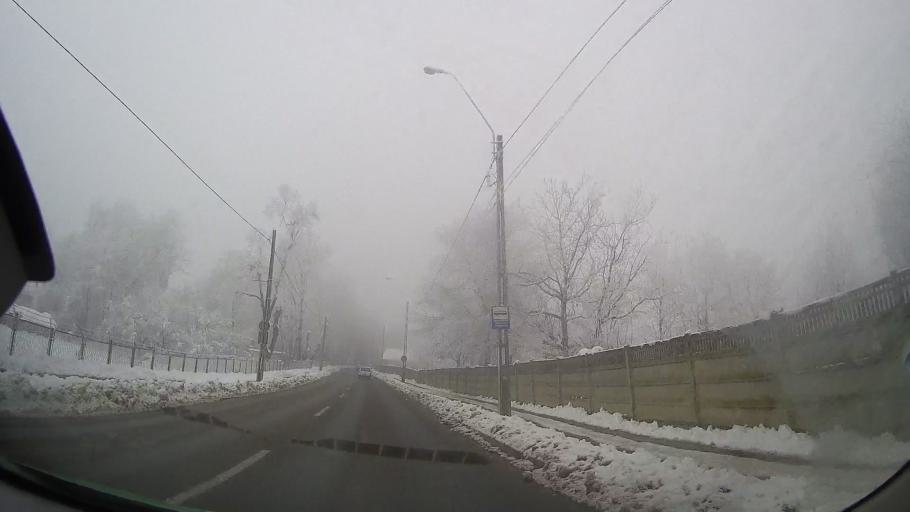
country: RO
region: Neamt
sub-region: Municipiul Roman
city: Roman
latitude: 46.9312
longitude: 26.9176
